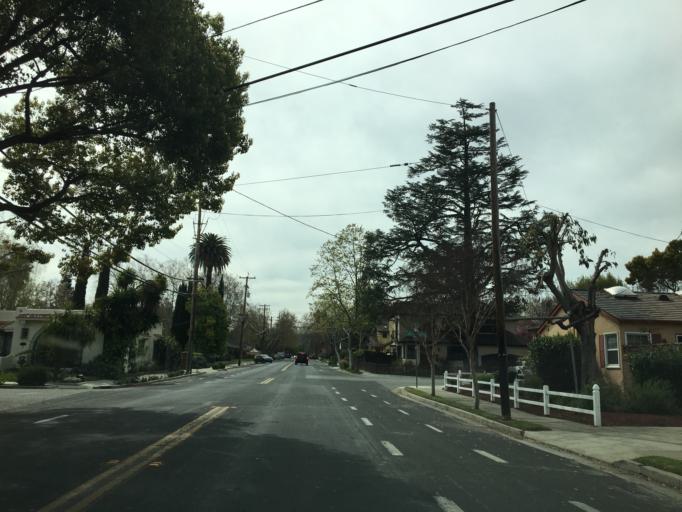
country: US
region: California
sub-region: Santa Clara County
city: Buena Vista
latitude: 37.3066
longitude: -121.9053
